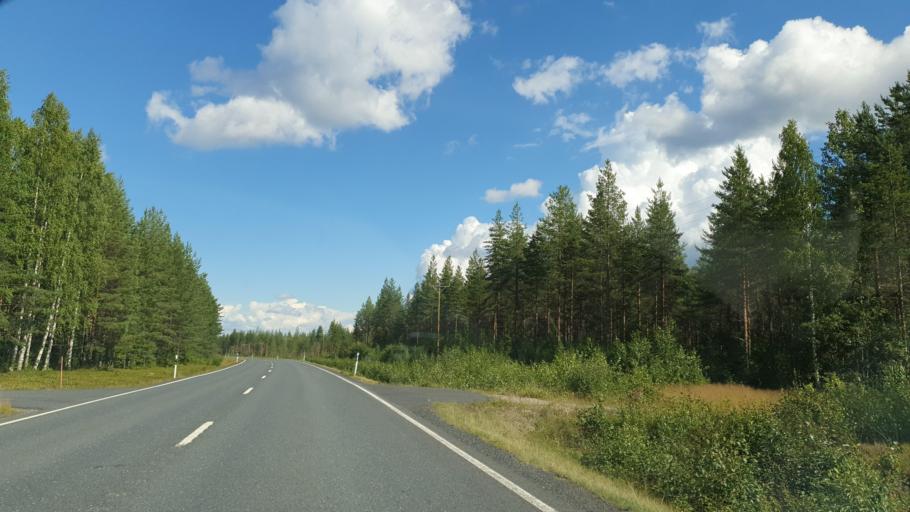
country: FI
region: Kainuu
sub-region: Kehys-Kainuu
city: Kuhmo
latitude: 64.0839
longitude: 29.0623
